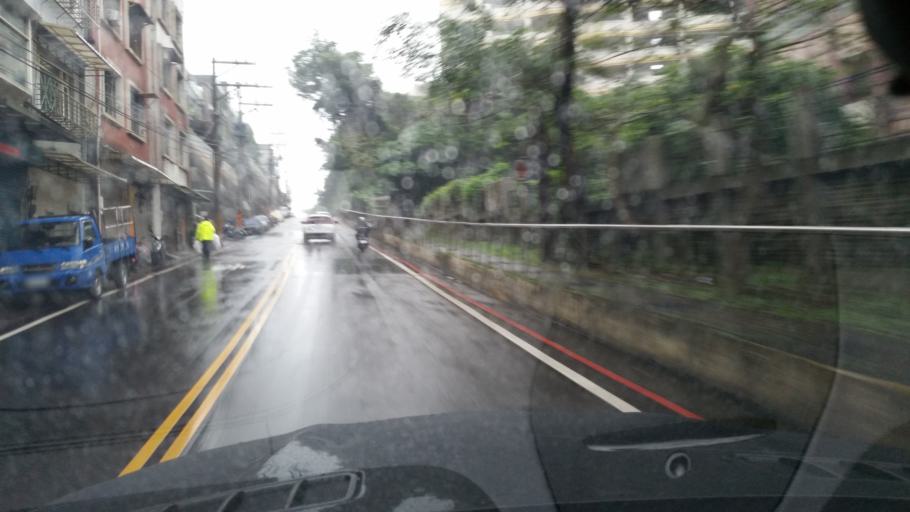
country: TW
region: Taiwan
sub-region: Keelung
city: Keelung
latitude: 25.1467
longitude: 121.7704
